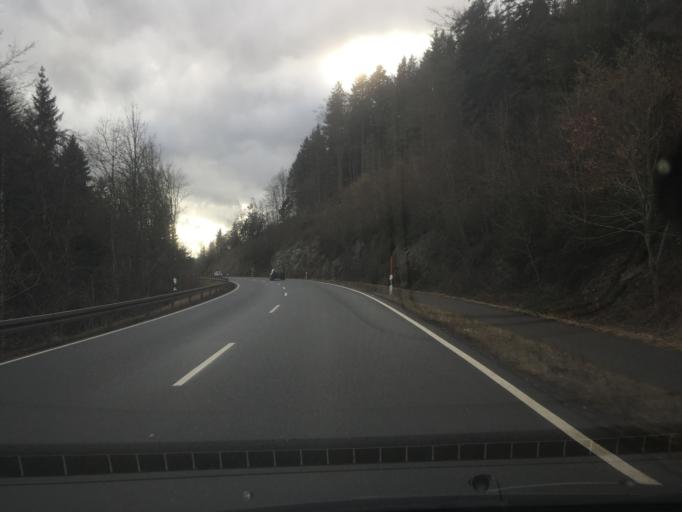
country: DE
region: Baden-Wuerttemberg
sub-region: Freiburg Region
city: Hausern
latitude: 47.7613
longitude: 8.1848
